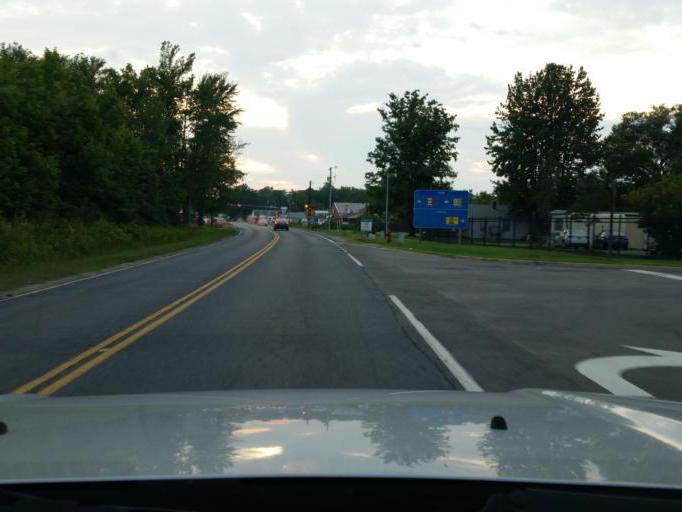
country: US
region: Virginia
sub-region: Spotsylvania County
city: Spotsylvania Courthouse
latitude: 38.1329
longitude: -77.5183
